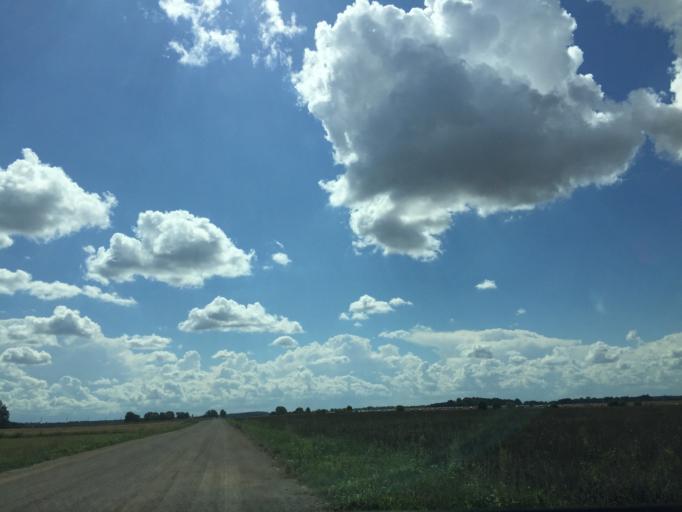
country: LV
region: Rundales
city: Pilsrundale
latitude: 56.3222
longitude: 23.9901
